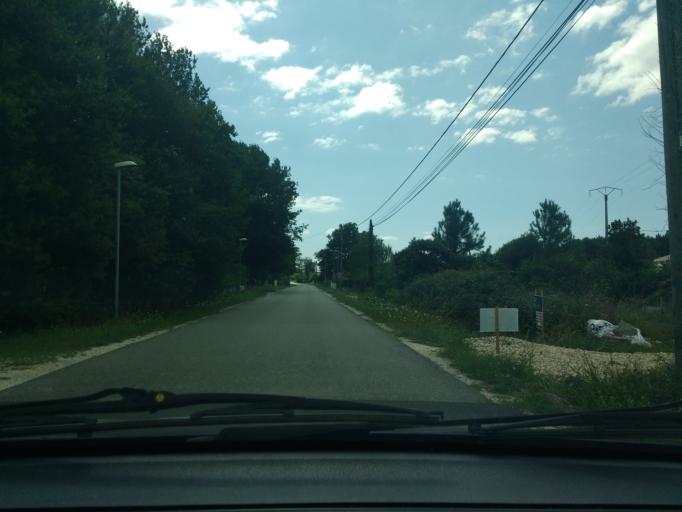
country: FR
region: Aquitaine
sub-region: Departement de la Gironde
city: Salles
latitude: 44.5626
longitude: -0.8469
